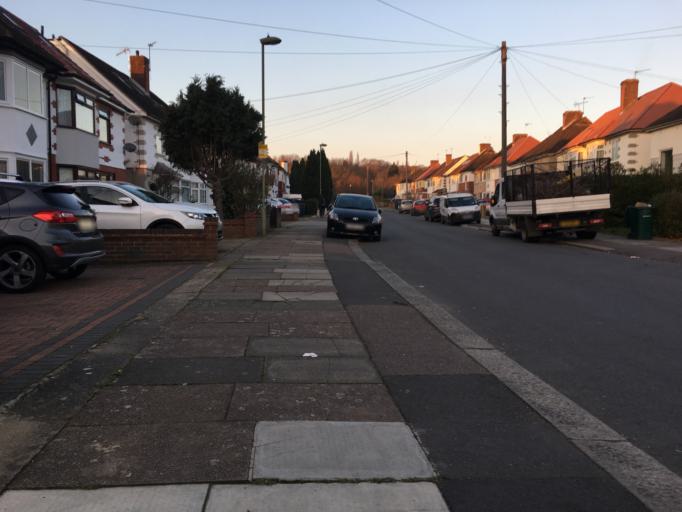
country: GB
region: England
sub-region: Greater London
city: Hendon
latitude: 51.6098
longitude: -0.2261
